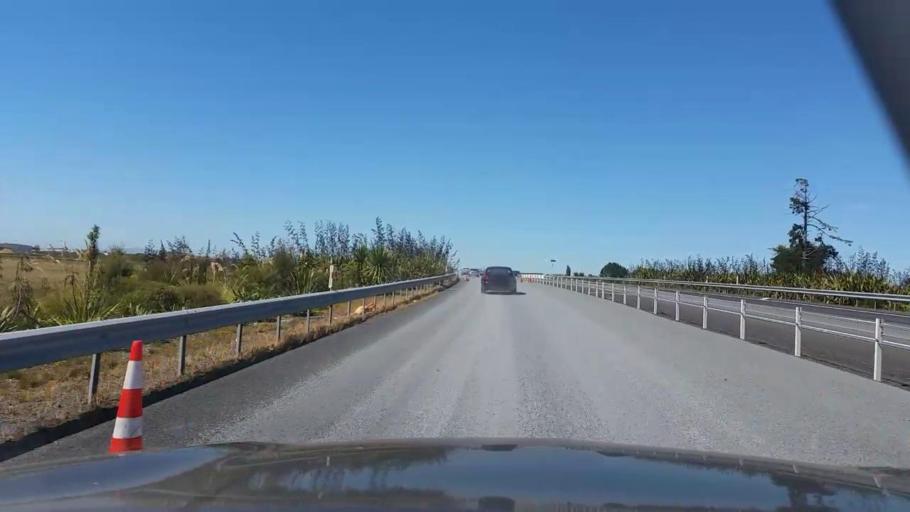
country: NZ
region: Waikato
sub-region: Hamilton City
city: Hamilton
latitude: -37.7465
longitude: 175.2152
